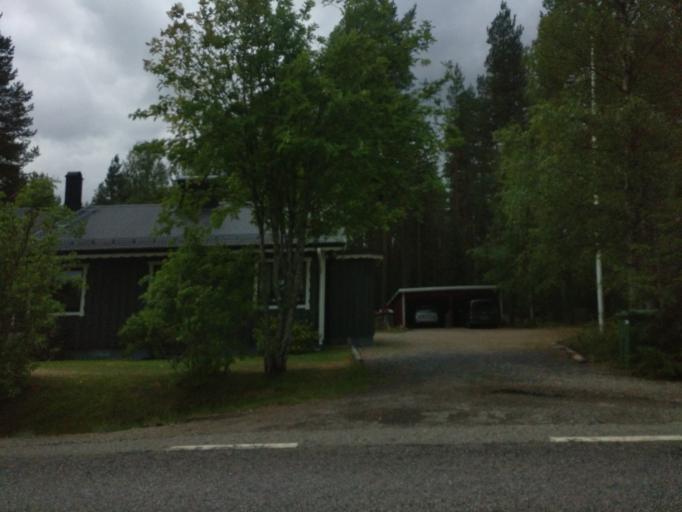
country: SE
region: Vaermland
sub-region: Torsby Kommun
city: Torsby
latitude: 60.7537
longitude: 12.7803
